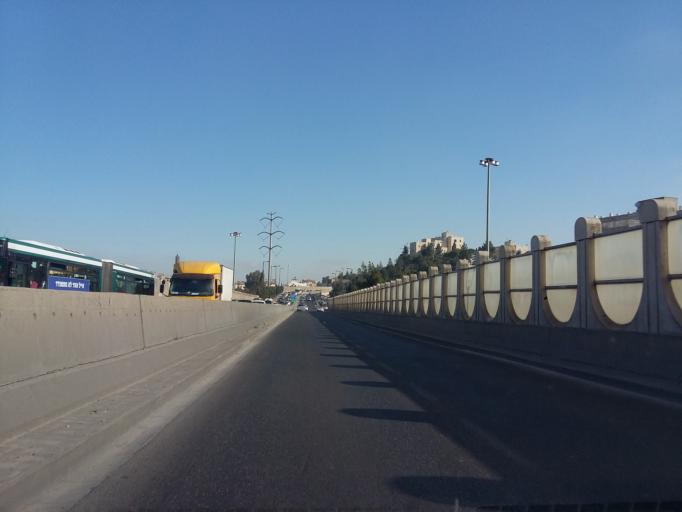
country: PS
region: West Bank
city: East Jerusalem
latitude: 31.8042
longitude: 35.2350
